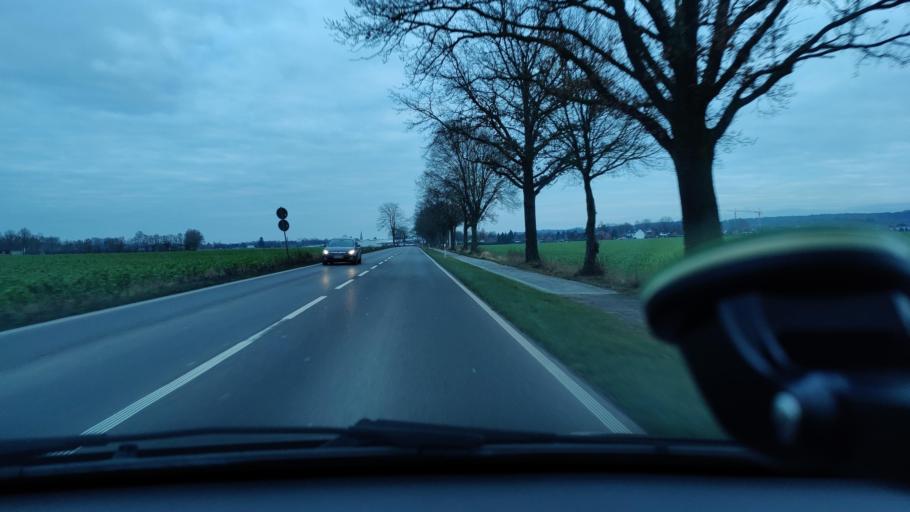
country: DE
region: North Rhine-Westphalia
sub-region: Regierungsbezirk Dusseldorf
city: Grefrath
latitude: 51.3096
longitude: 6.3543
